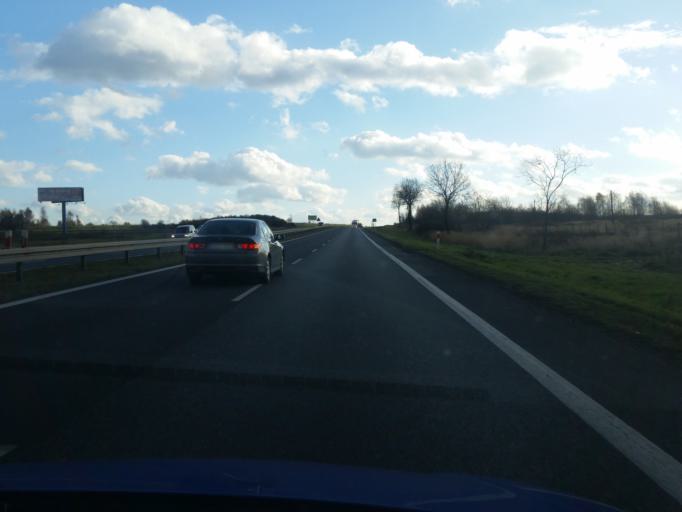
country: PL
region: Silesian Voivodeship
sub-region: Powiat myszkowski
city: Kozieglowy
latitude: 50.5858
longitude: 19.1630
